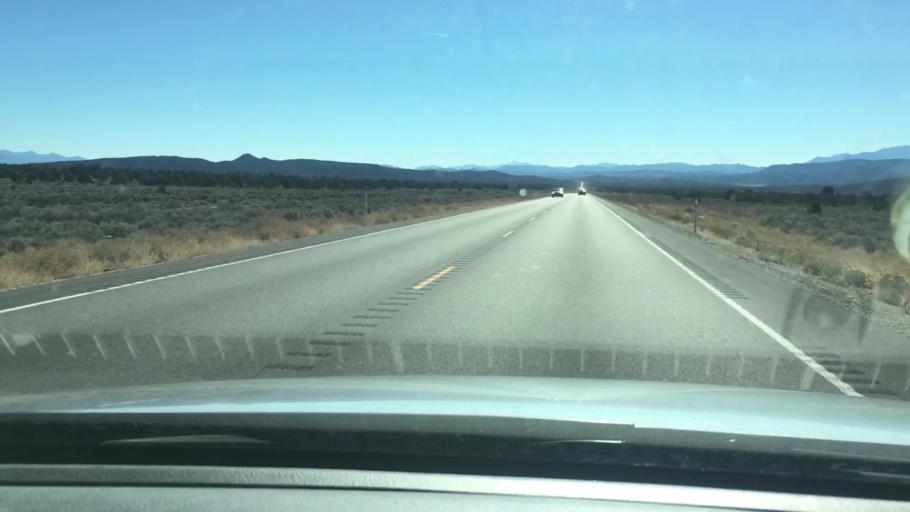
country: US
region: Nevada
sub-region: White Pine County
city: Ely
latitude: 39.1596
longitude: -115.0271
